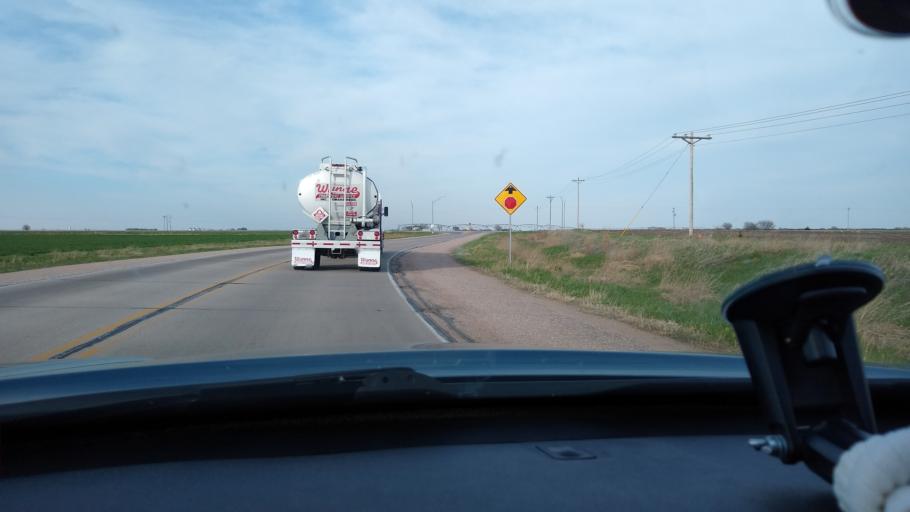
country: US
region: Nebraska
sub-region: Fillmore County
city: Geneva
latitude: 40.5555
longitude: -97.5949
